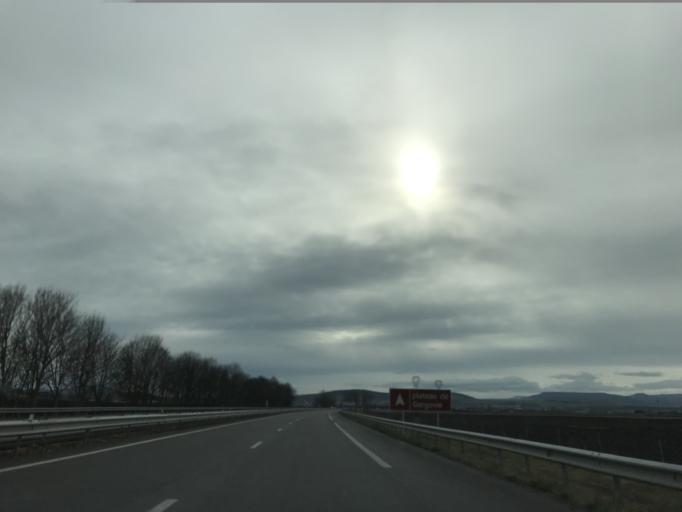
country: FR
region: Auvergne
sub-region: Departement du Puy-de-Dome
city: Pont-du-Chateau
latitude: 45.8135
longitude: 3.2225
